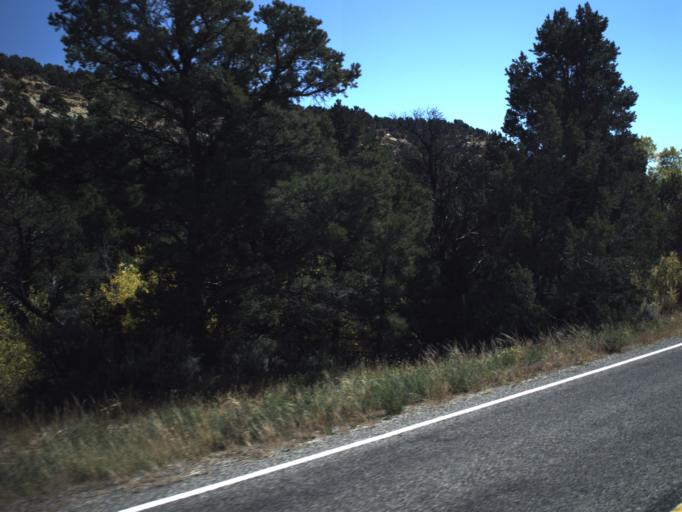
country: US
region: Utah
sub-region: Wayne County
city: Loa
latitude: 37.9280
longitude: -111.4280
